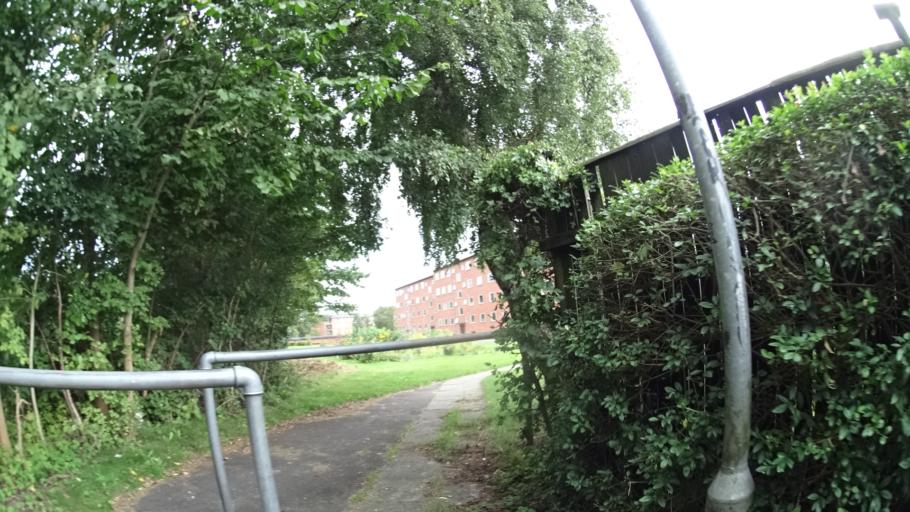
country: DK
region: Central Jutland
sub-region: Arhus Kommune
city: Stavtrup
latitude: 56.1524
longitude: 10.1185
